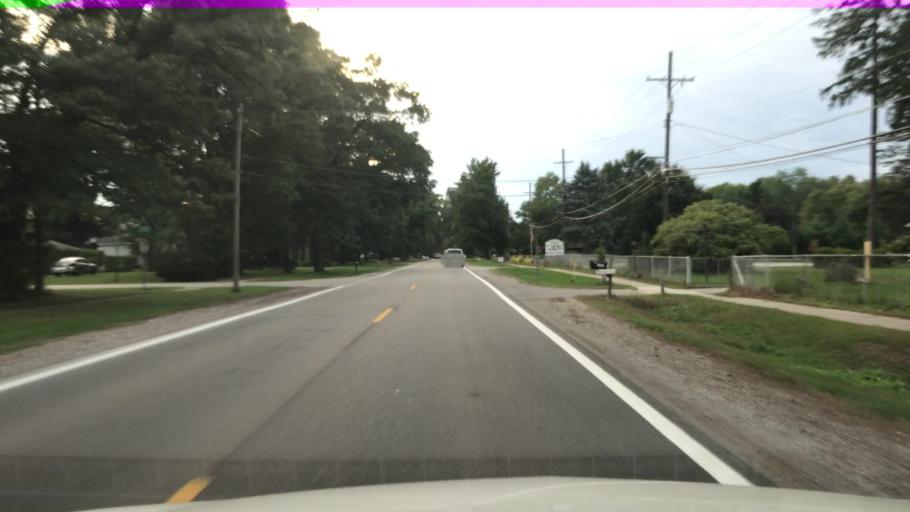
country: US
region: Michigan
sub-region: Macomb County
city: Shelby
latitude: 42.6831
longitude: -83.0700
